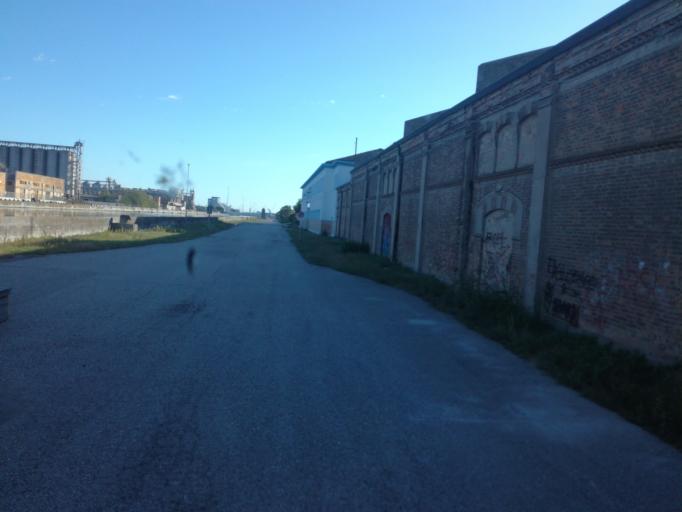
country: IT
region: Emilia-Romagna
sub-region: Provincia di Ravenna
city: Ravenna
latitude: 44.4231
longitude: 12.2159
